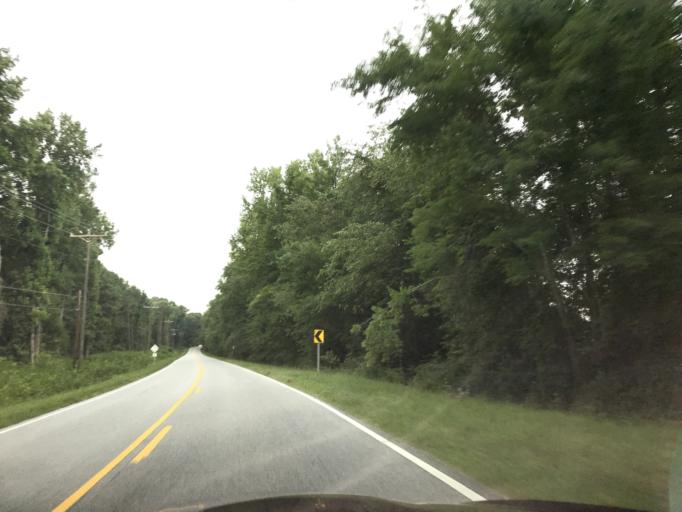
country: US
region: North Carolina
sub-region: Johnston County
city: Wilsons Mills
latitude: 35.5504
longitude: -78.3887
